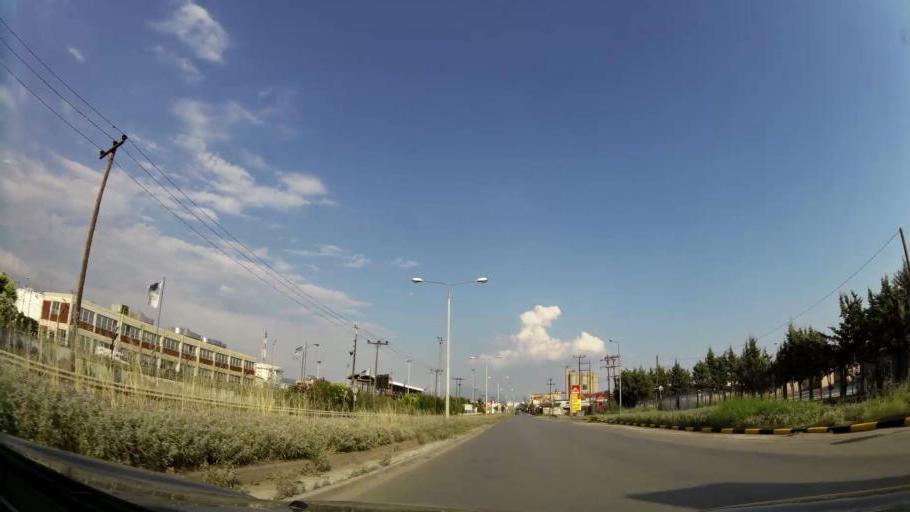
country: GR
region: Central Macedonia
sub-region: Nomos Thessalonikis
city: Diavata
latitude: 40.6755
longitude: 22.8758
